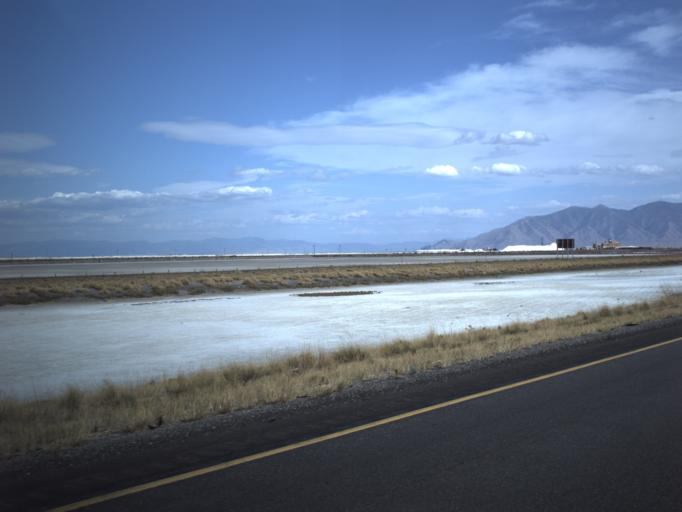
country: US
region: Utah
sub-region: Tooele County
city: Grantsville
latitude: 40.7130
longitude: -112.5387
